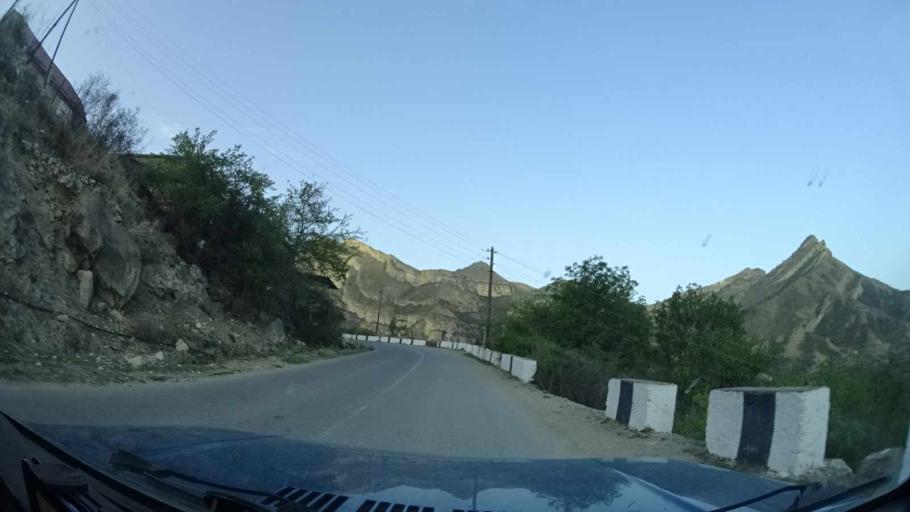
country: RU
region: Dagestan
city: Gunib
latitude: 42.3819
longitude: 46.9632
